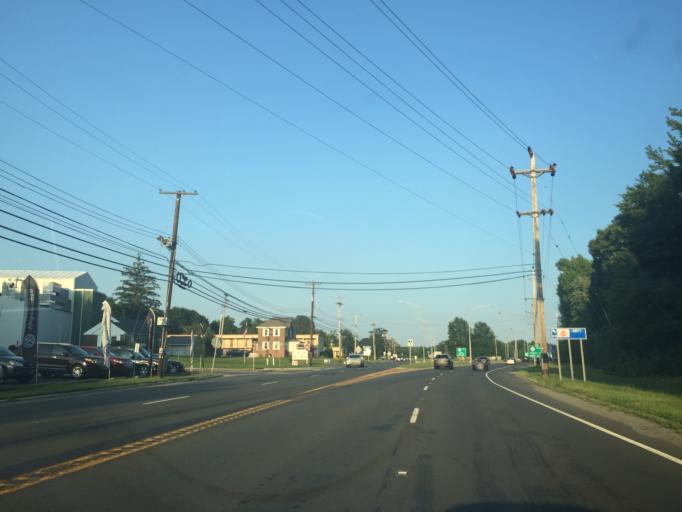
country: US
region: New Jersey
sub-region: Monmouth County
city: Shark River Hills
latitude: 40.2178
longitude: -74.1071
